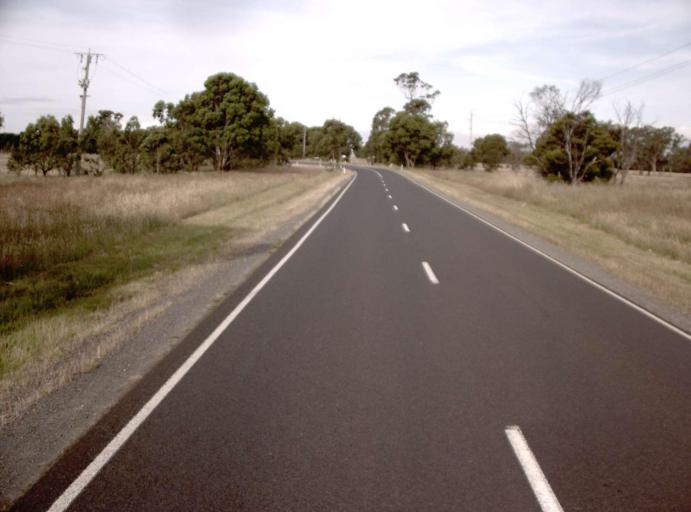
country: AU
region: Victoria
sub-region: Wellington
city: Heyfield
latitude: -38.0592
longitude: 146.6592
